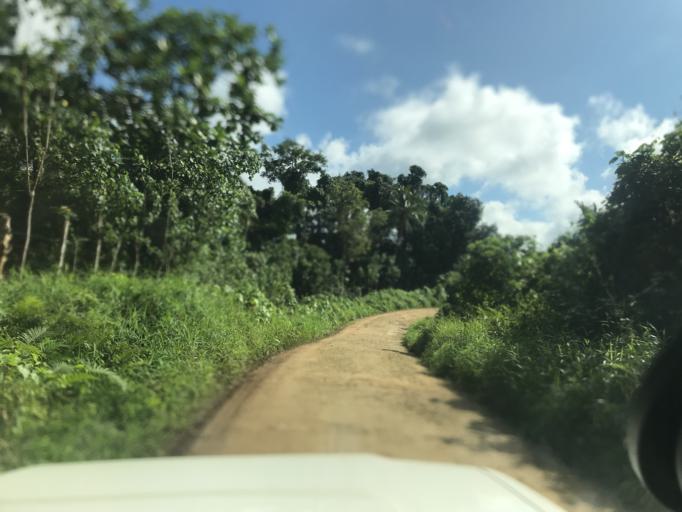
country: VU
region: Sanma
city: Luganville
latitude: -15.4664
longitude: 167.0712
